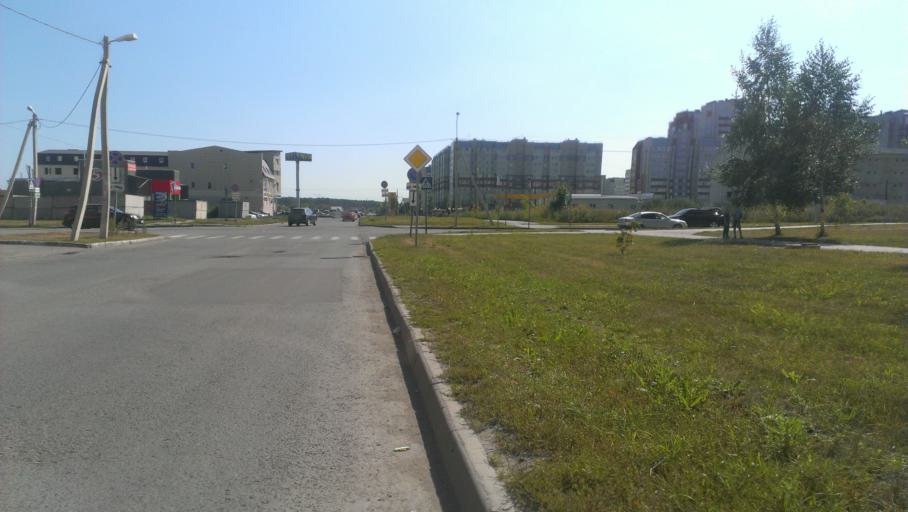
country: RU
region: Altai Krai
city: Novosilikatnyy
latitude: 53.3304
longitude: 83.6843
